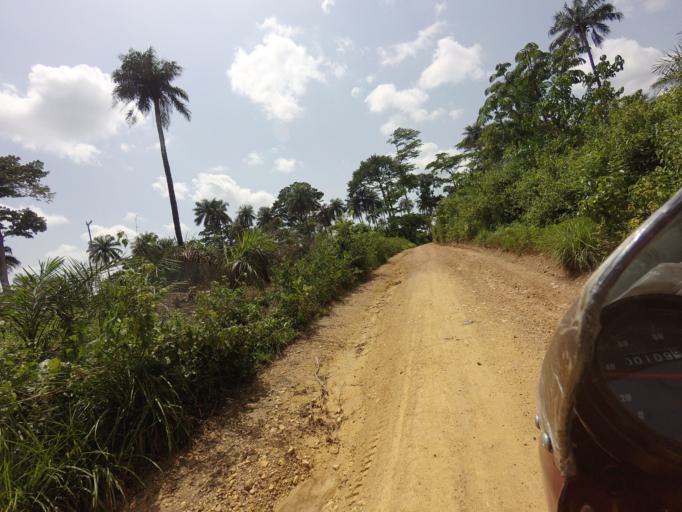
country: SL
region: Eastern Province
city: Bunumbu
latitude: 8.1304
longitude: -10.8203
